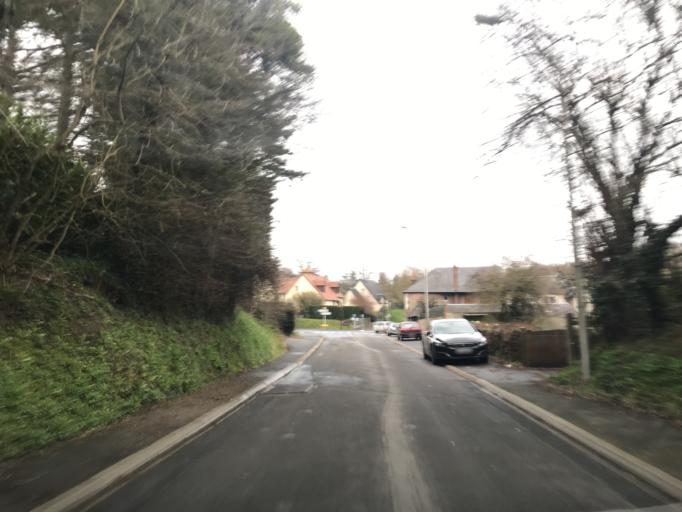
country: FR
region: Lower Normandy
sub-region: Departement du Calvados
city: Dozule
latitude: 49.2304
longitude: -0.0506
